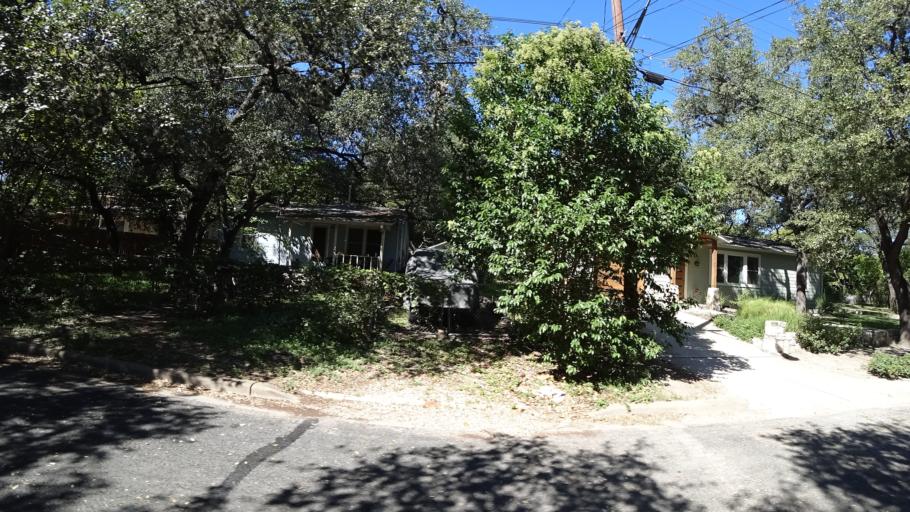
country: US
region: Texas
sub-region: Travis County
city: Austin
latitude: 30.2395
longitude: -97.7633
